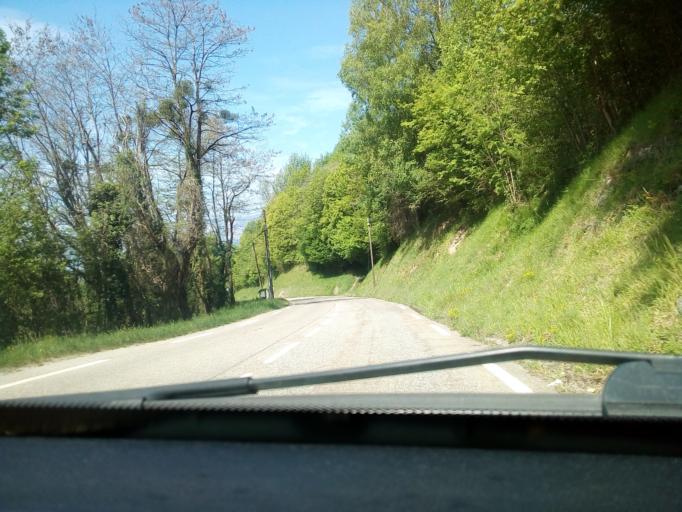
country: FR
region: Rhone-Alpes
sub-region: Departement de l'Isere
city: Le Champ-pres-Froges
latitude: 45.2707
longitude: 5.9486
